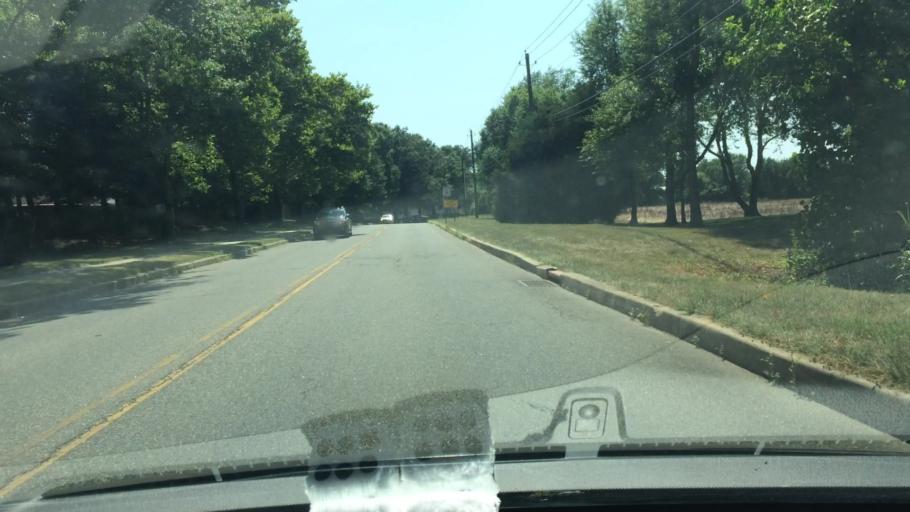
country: US
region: New Jersey
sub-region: Gloucester County
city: Beckett
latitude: 39.7556
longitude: -75.3592
